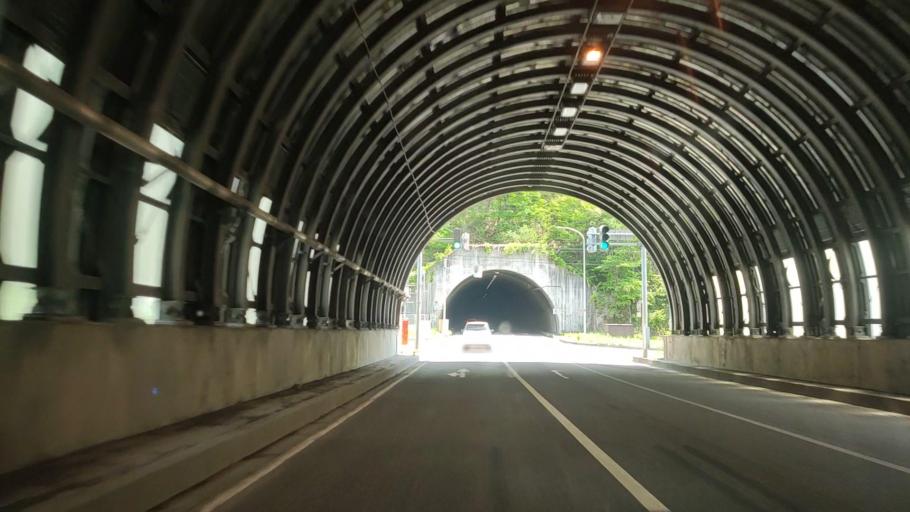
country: JP
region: Nagano
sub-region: Kitaazumi Gun
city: Hakuba
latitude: 36.8133
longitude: 137.9108
